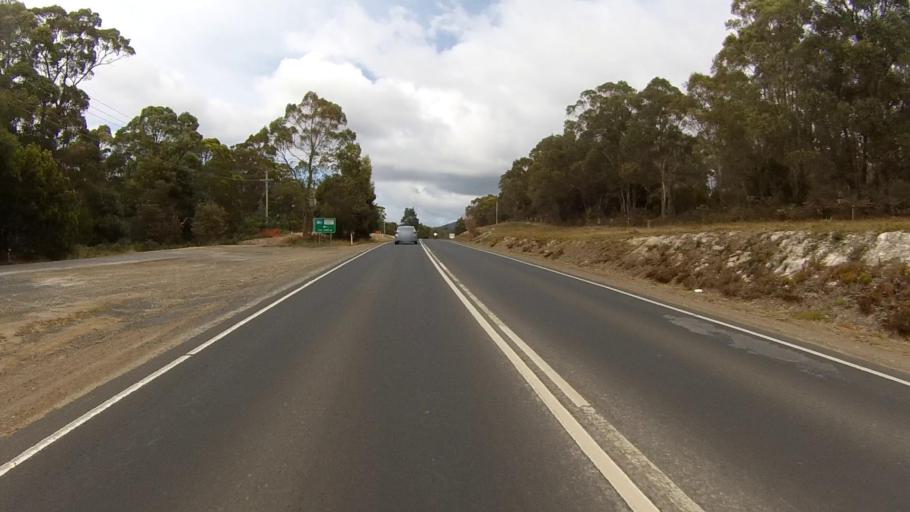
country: AU
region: Tasmania
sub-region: Kingborough
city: Margate
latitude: -43.0450
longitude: 147.2654
